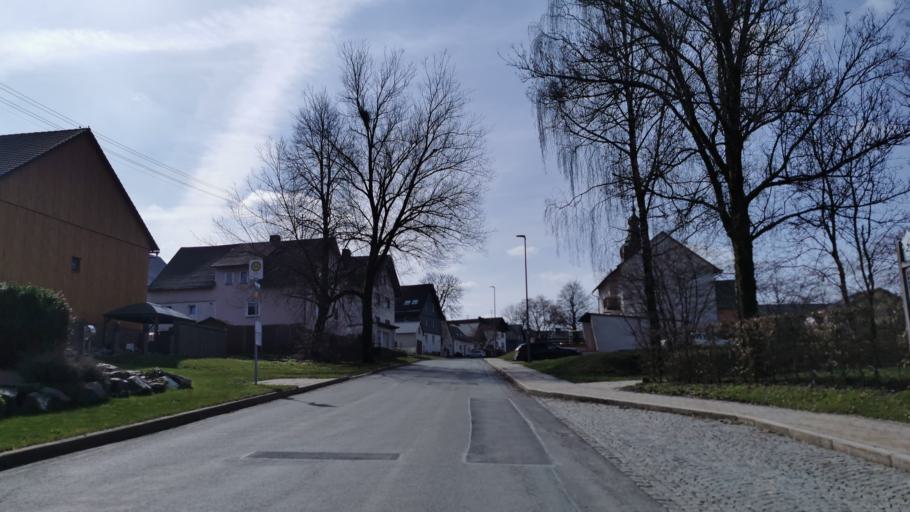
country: DE
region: Bavaria
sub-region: Upper Franconia
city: Teuschnitz
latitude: 50.4134
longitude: 11.3367
